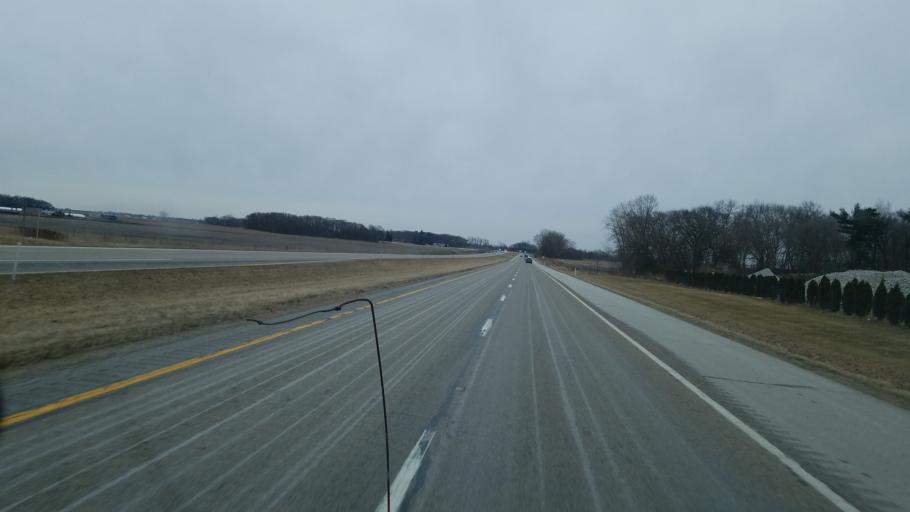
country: US
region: Indiana
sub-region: LaPorte County
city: Kingsford Heights
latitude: 41.4169
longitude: -86.7795
